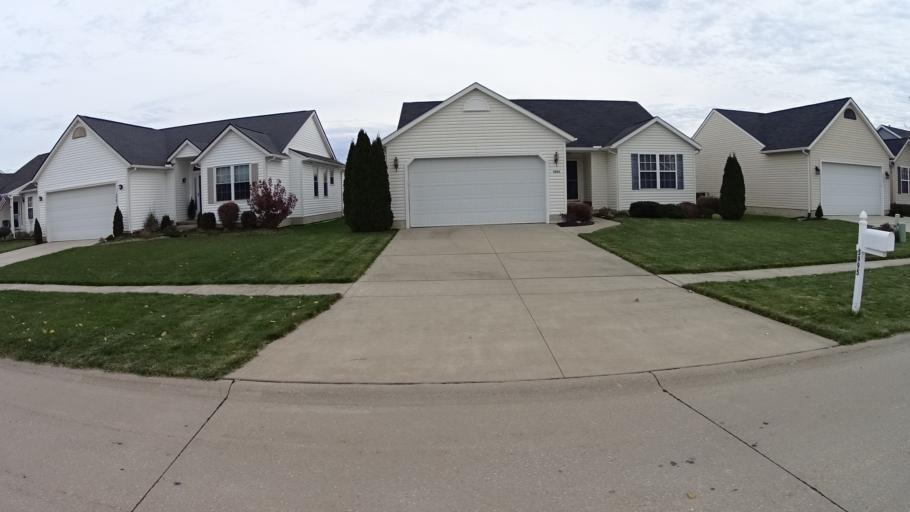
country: US
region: Ohio
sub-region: Lorain County
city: North Ridgeville
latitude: 41.4033
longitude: -82.0431
